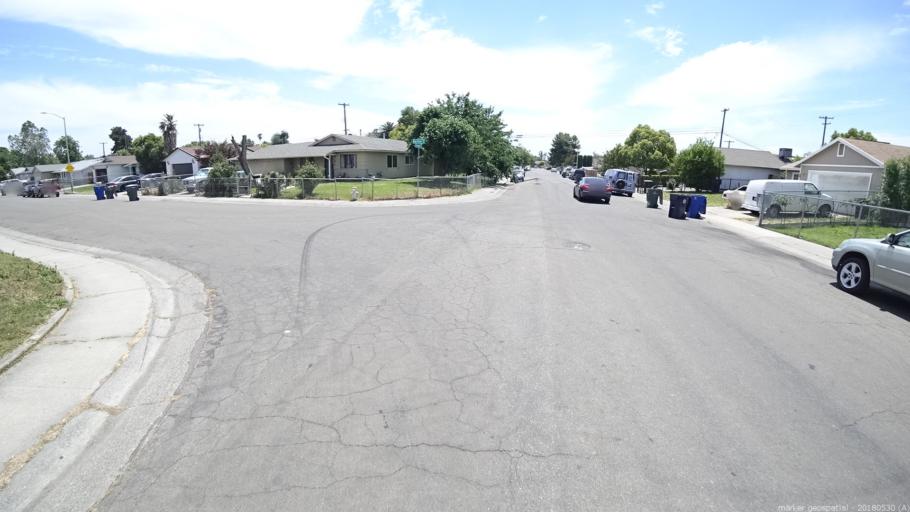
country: US
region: California
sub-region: Sacramento County
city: Sacramento
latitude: 38.6247
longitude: -121.4668
